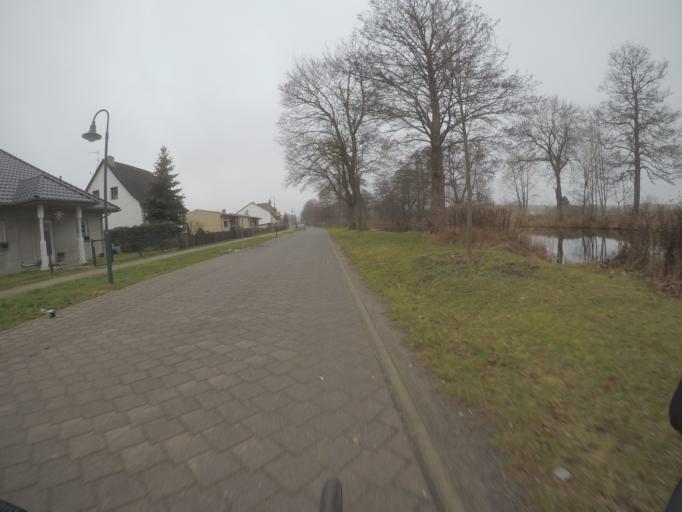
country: DE
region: Brandenburg
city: Marienwerder
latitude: 52.8492
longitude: 13.5338
